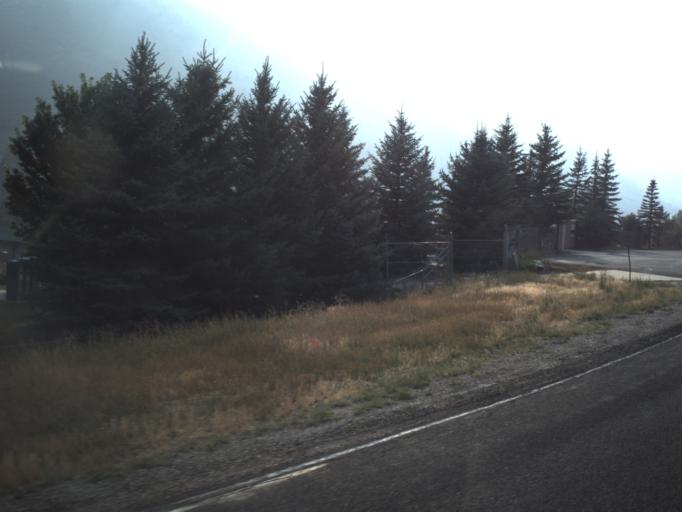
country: US
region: Utah
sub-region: Summit County
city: Francis
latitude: 40.6246
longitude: -111.2267
